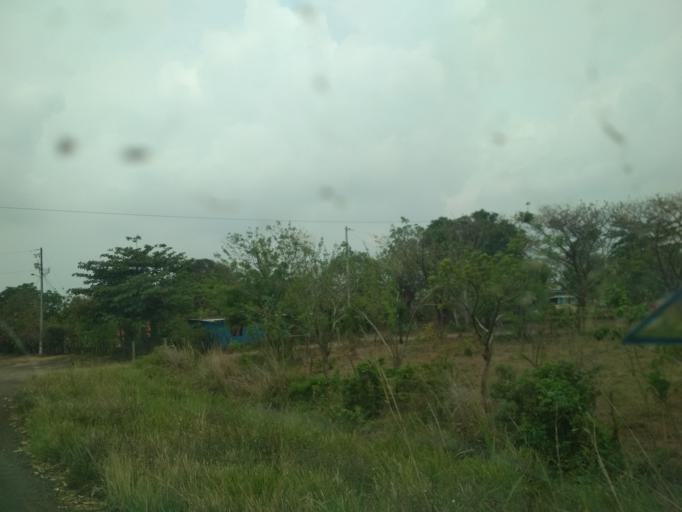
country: MX
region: Veracruz
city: Paso del Toro
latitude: 19.0147
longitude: -96.1424
